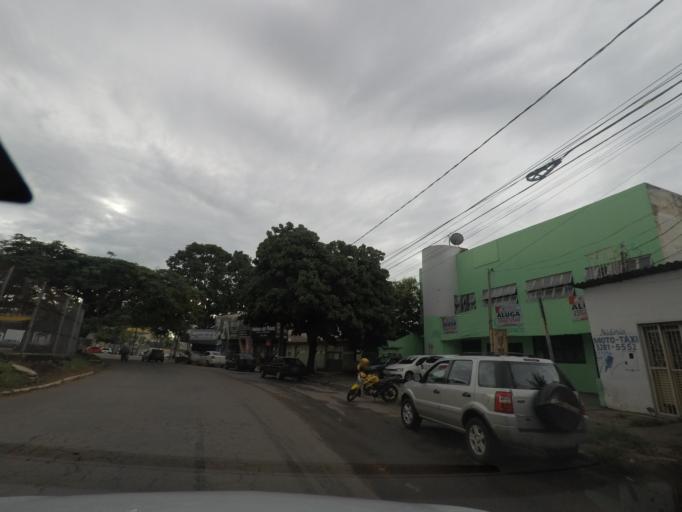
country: BR
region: Goias
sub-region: Goiania
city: Goiania
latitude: -16.7134
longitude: -49.2523
